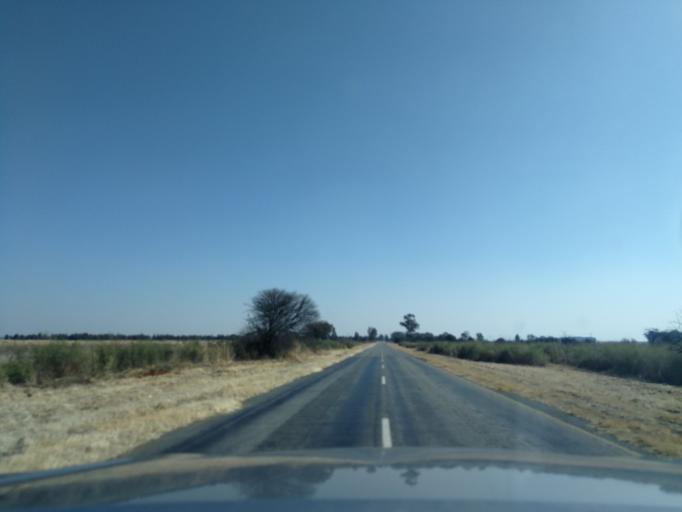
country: ZA
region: Orange Free State
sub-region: Fezile Dabi District Municipality
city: Viljoenskroon
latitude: -27.3582
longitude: 27.0222
